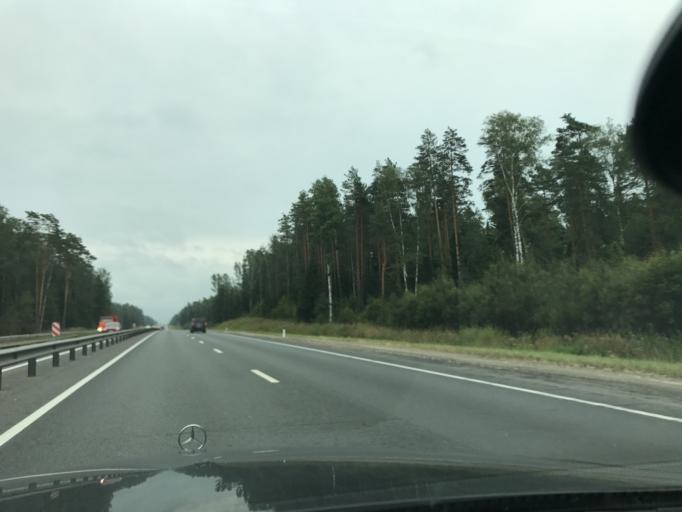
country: RU
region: Vladimir
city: Melekhovo
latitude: 56.2136
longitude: 41.3570
